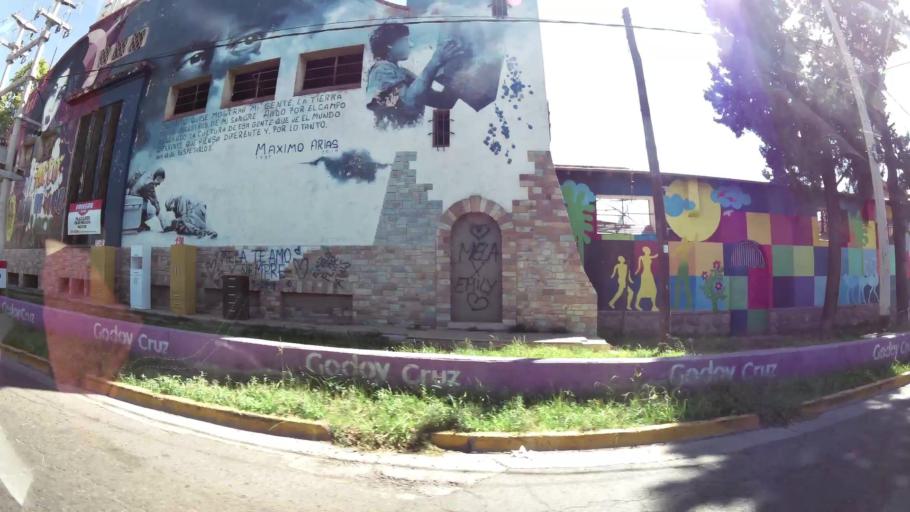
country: AR
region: Mendoza
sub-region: Departamento de Godoy Cruz
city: Godoy Cruz
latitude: -32.9537
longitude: -68.8370
